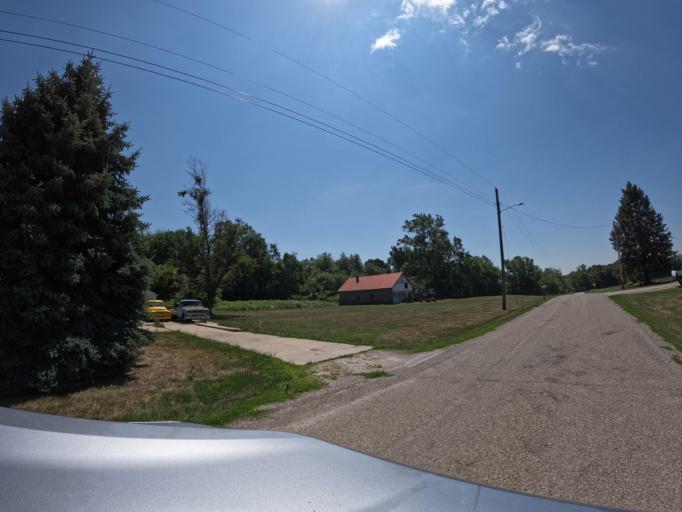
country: US
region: Iowa
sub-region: Keokuk County
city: Sigourney
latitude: 41.2614
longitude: -92.2502
